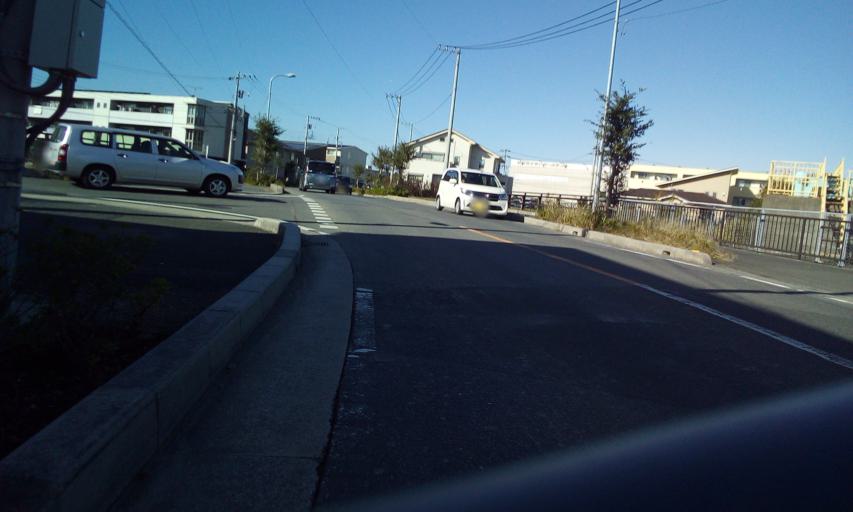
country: JP
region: Saitama
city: Yoshikawa
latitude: 35.8644
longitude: 139.8588
